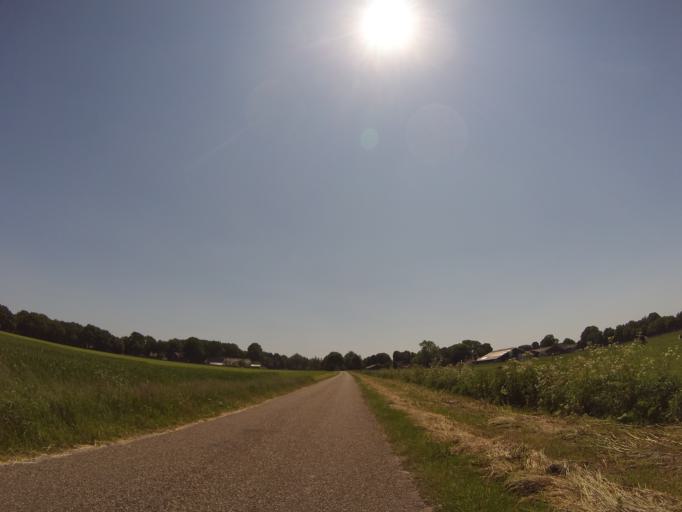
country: NL
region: Drenthe
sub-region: Gemeente Coevorden
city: Sleen
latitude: 52.7587
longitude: 6.8232
